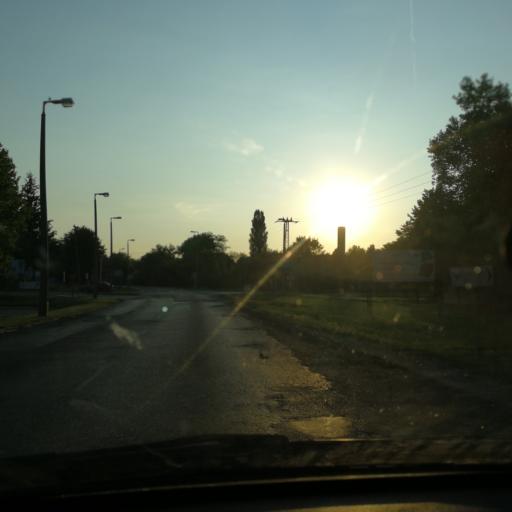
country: HU
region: Bacs-Kiskun
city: Kiskunhalas
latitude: 46.4331
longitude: 19.4984
